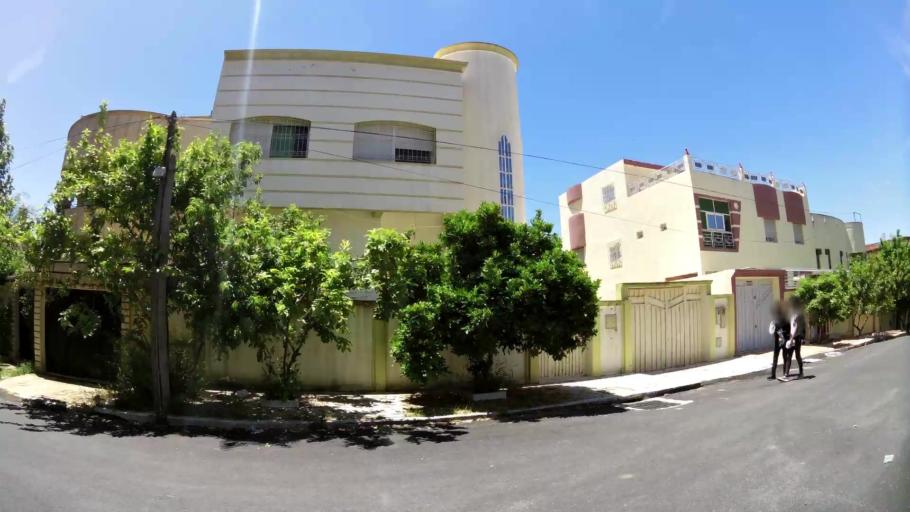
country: MA
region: Meknes-Tafilalet
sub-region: Meknes
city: Meknes
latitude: 33.9086
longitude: -5.5504
